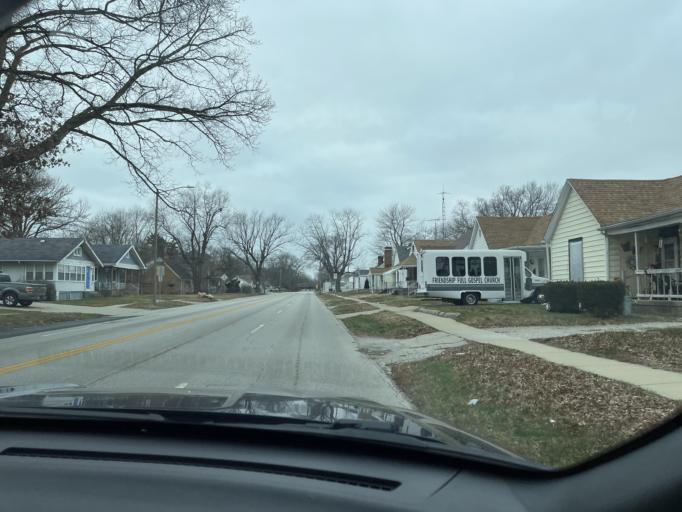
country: US
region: Illinois
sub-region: Sangamon County
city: Springfield
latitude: 39.7947
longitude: -89.6257
